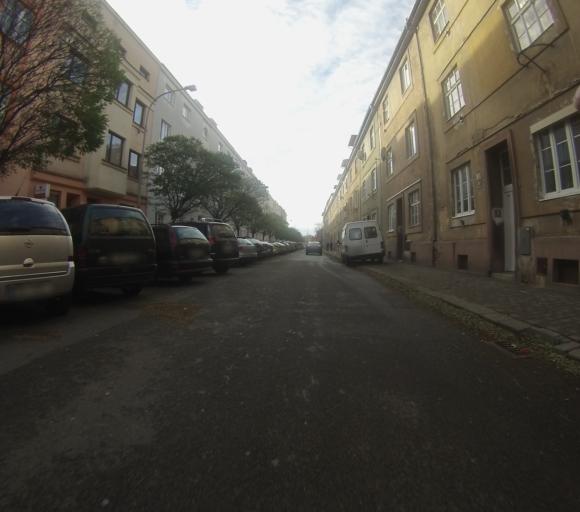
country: CZ
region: South Moravian
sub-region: Mesto Brno
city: Brno
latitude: 49.2005
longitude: 16.6341
